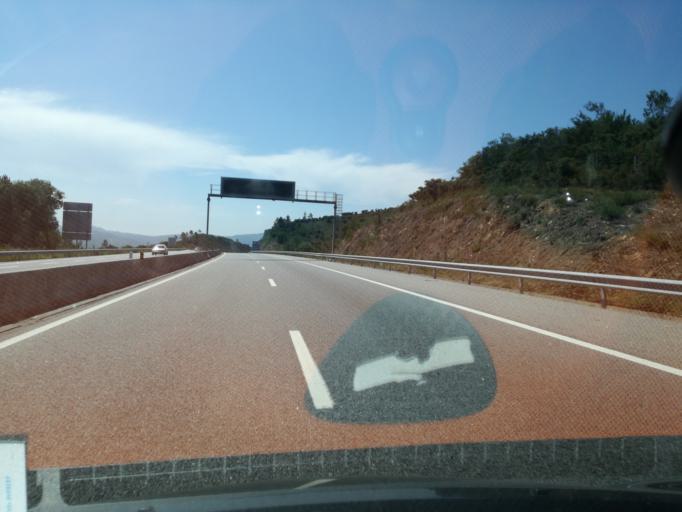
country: PT
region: Viana do Castelo
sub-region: Caminha
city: Vila Praia de Ancora
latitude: 41.8348
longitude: -8.7863
